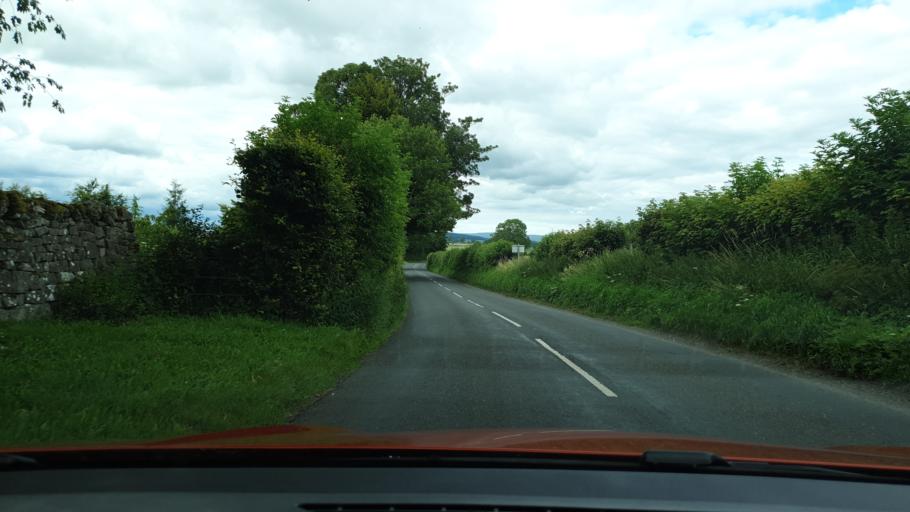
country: GB
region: England
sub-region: Cumbria
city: Penrith
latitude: 54.6196
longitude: -2.8017
